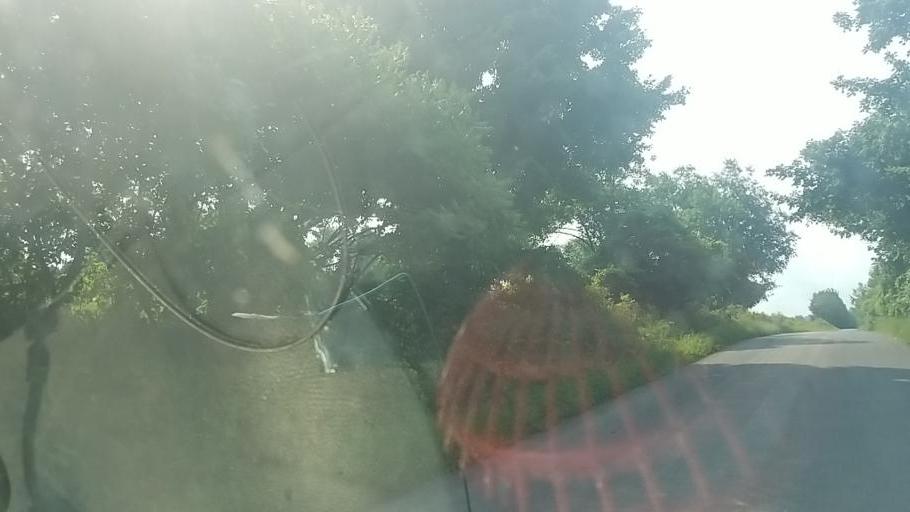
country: US
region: New York
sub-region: Montgomery County
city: Fonda
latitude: 42.9820
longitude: -74.4465
